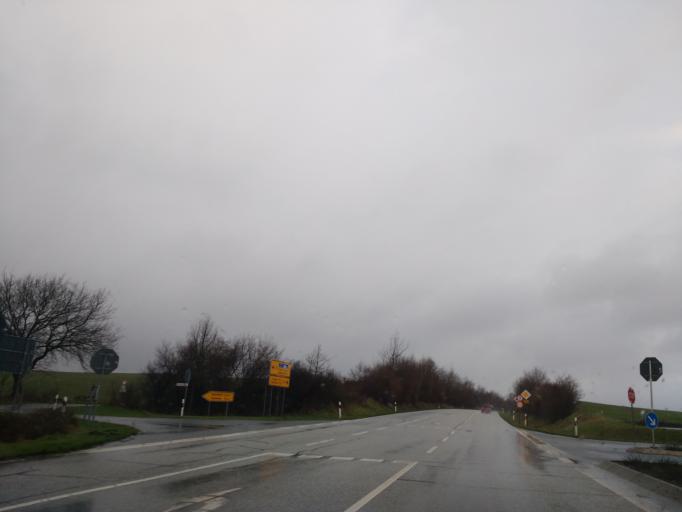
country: DE
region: Schleswig-Holstein
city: Klein Wittensee
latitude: 54.3914
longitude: 9.7289
